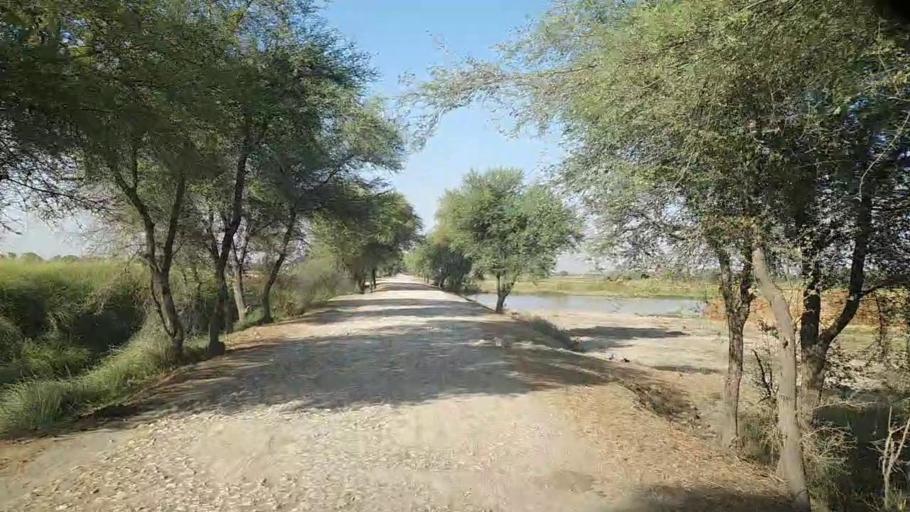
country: PK
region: Sindh
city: Tangwani
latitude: 28.2821
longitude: 68.9844
